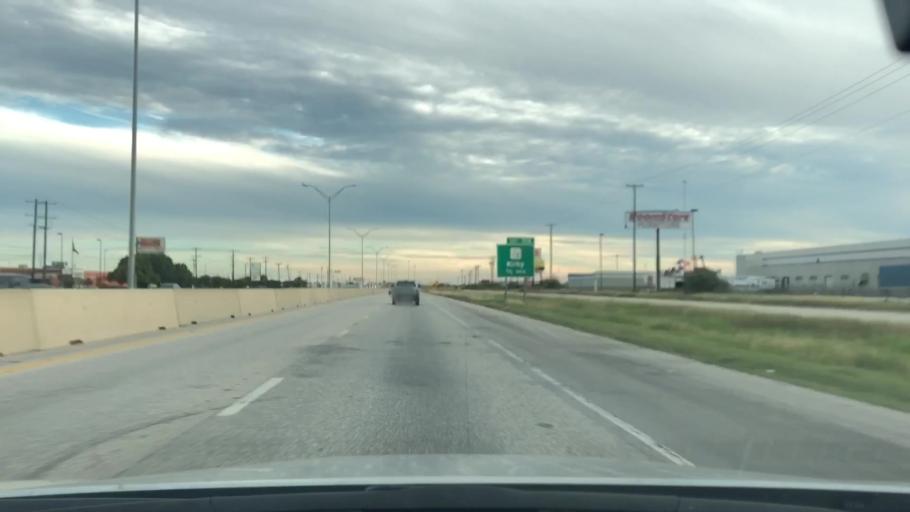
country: US
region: Texas
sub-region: Bexar County
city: Kirby
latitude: 29.4670
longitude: -98.4043
